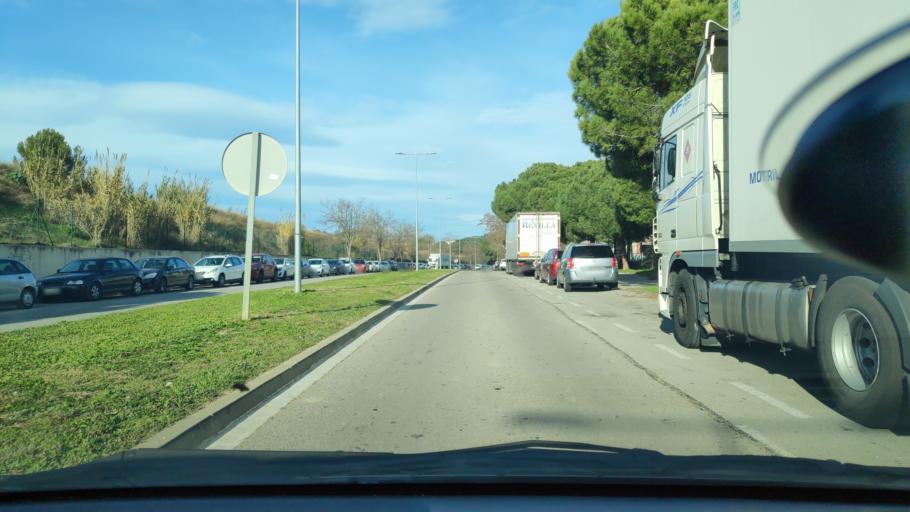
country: ES
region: Catalonia
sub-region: Provincia de Barcelona
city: Rubi
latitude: 41.4888
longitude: 2.0475
